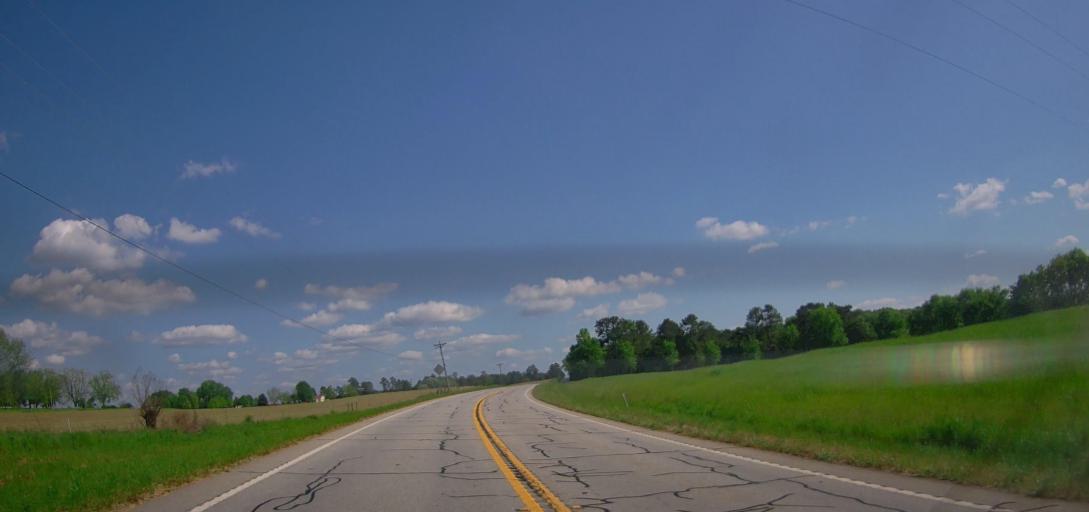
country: US
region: Georgia
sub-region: Greene County
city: Greensboro
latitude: 33.6114
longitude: -83.3123
